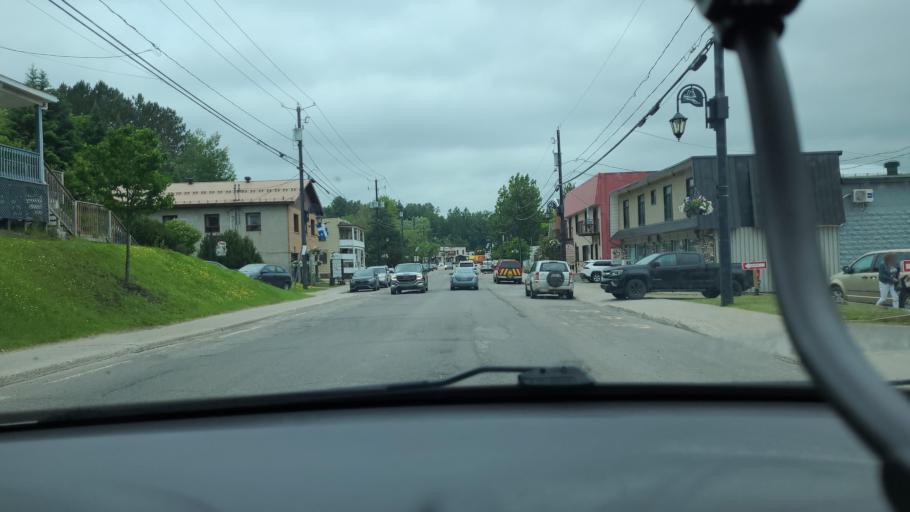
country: CA
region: Quebec
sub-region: Laurentides
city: Riviere-Rouge
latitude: 46.4076
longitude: -74.8681
